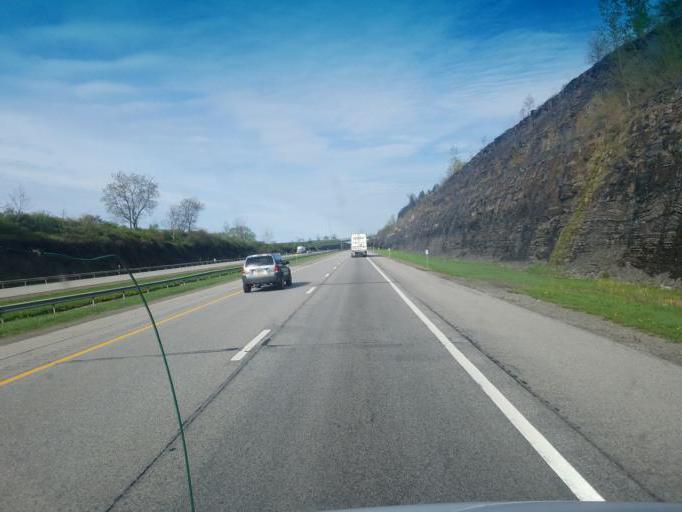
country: US
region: New York
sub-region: Herkimer County
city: Little Falls
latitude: 43.0082
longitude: -74.8695
